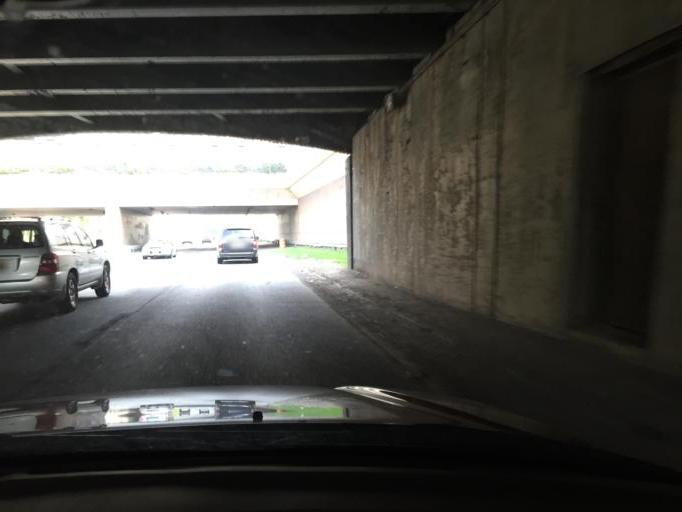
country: US
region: New York
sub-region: Bronx
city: The Bronx
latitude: 40.8408
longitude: -73.8385
